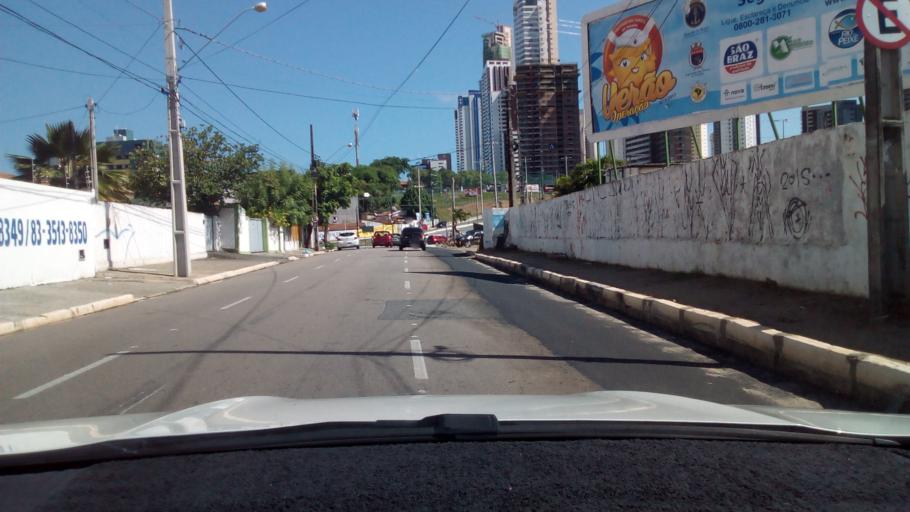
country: BR
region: Paraiba
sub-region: Joao Pessoa
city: Joao Pessoa
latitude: -7.1240
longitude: -34.8285
